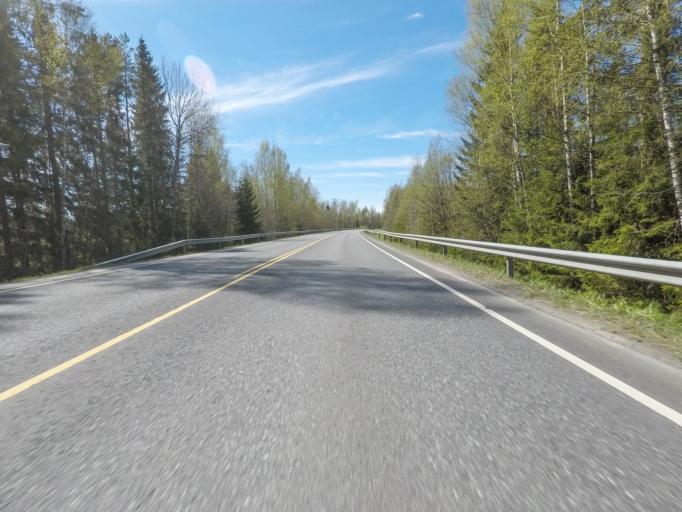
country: FI
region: Haeme
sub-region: Forssa
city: Humppila
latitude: 60.9814
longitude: 23.4395
